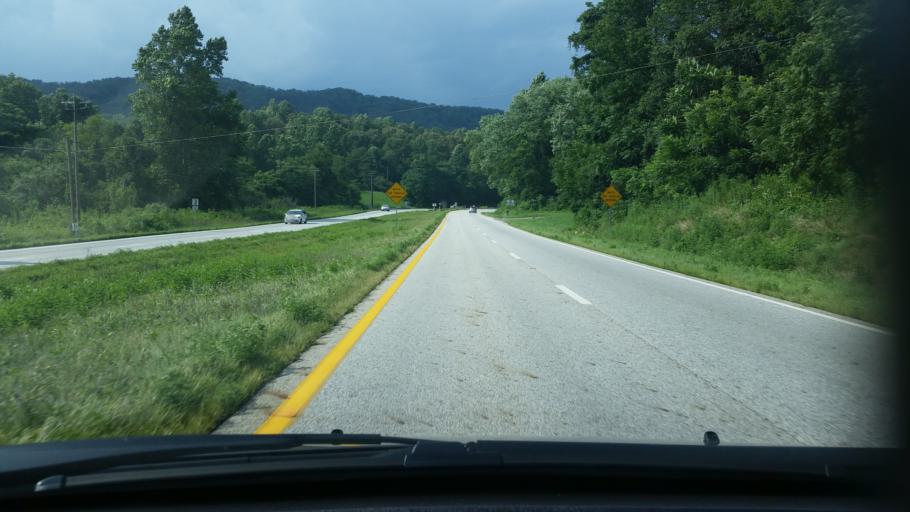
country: US
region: Virginia
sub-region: Nelson County
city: Lovingston
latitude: 37.8023
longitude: -78.8620
